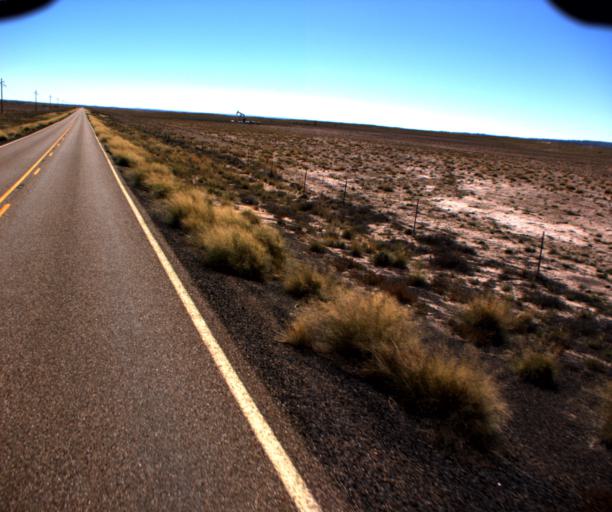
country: US
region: Arizona
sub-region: Navajo County
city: Holbrook
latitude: 35.1152
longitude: -110.0936
